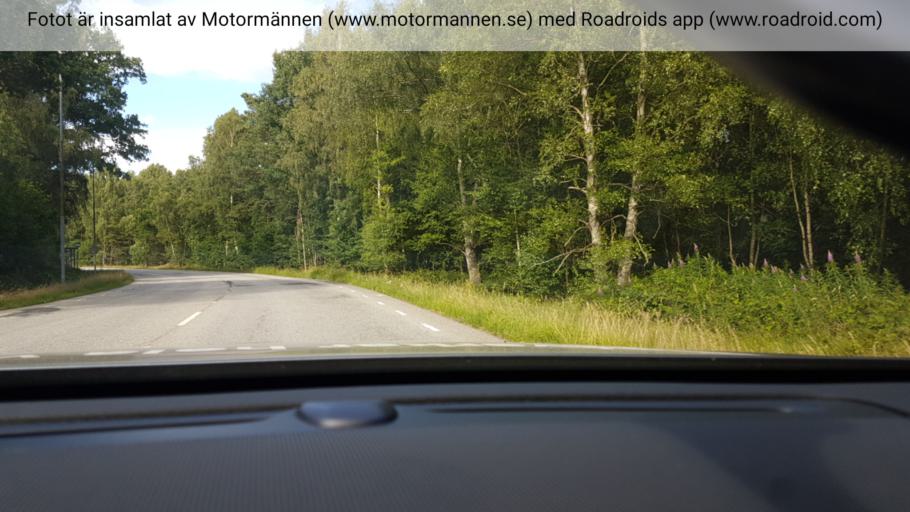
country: SE
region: Skane
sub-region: Hassleholms Kommun
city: Hassleholm
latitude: 56.1706
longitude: 13.8018
